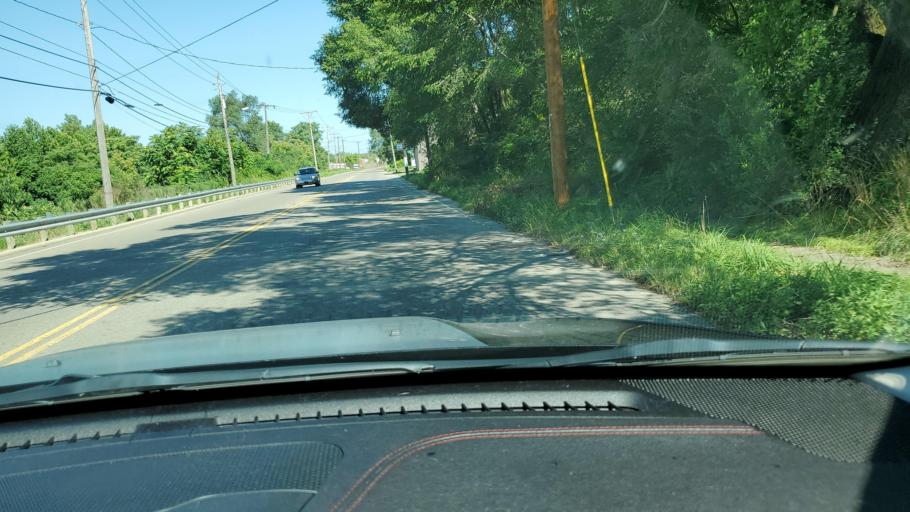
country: US
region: Ohio
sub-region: Mahoning County
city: Campbell
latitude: 41.0696
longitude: -80.5966
